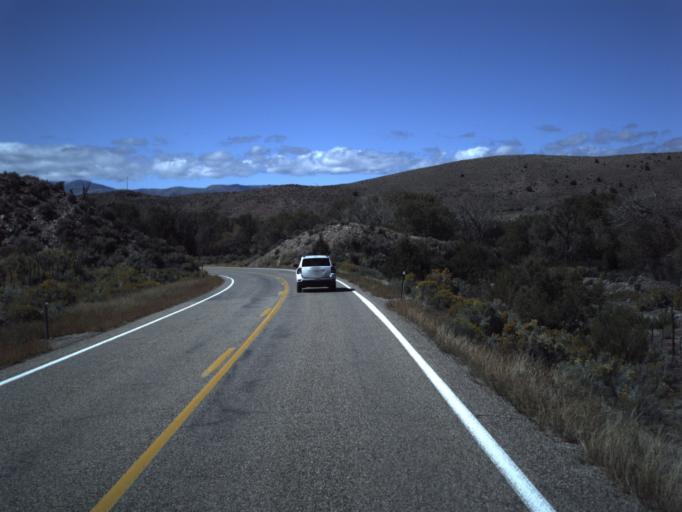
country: US
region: Utah
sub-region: Piute County
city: Junction
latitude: 38.2035
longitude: -112.1604
